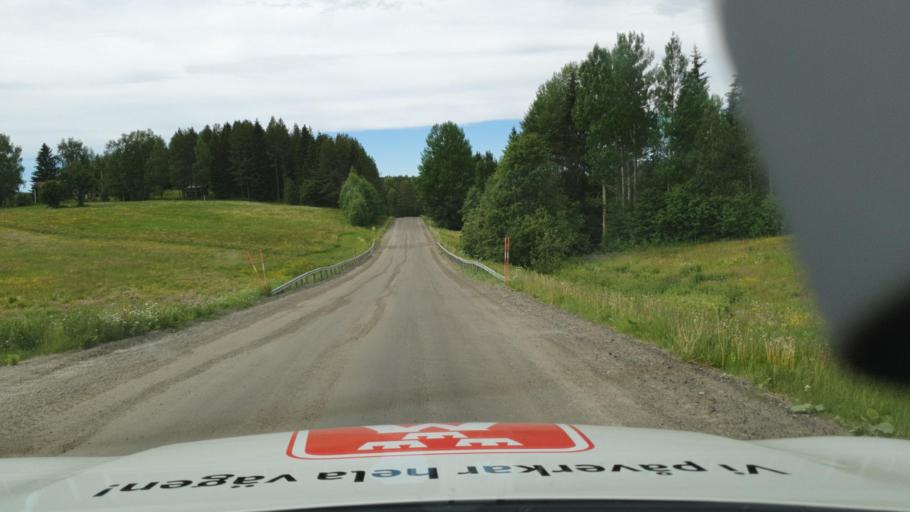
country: SE
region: Vaesterbotten
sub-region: Skelleftea Kommun
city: Burtraesk
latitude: 64.3606
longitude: 20.4194
